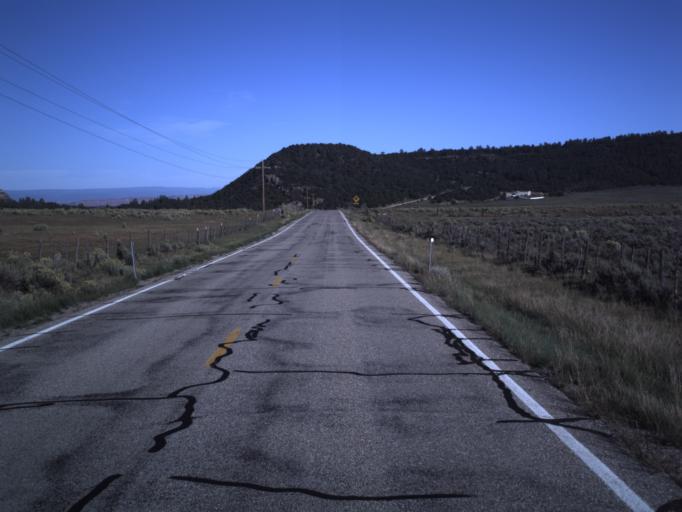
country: US
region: Utah
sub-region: Grand County
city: Moab
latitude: 38.3286
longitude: -109.1369
